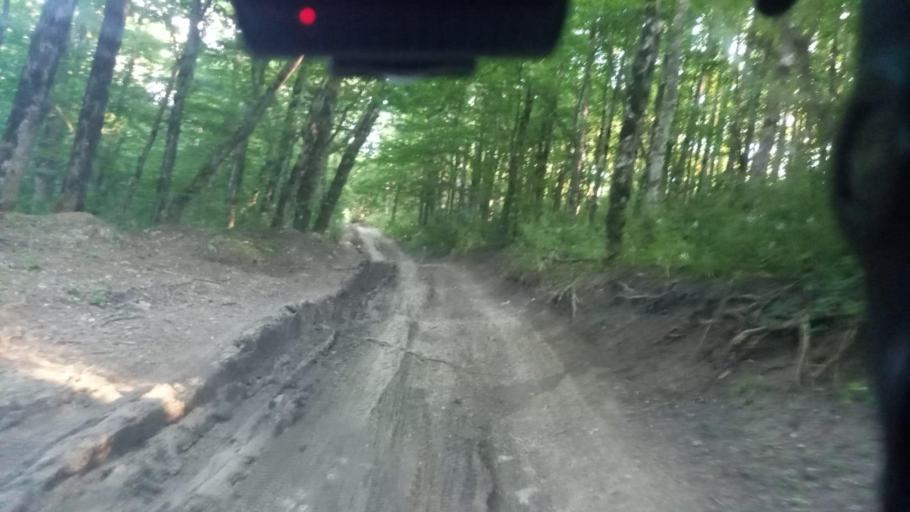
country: RU
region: Krasnodarskiy
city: Gelendzhik
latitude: 44.6205
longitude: 38.1880
